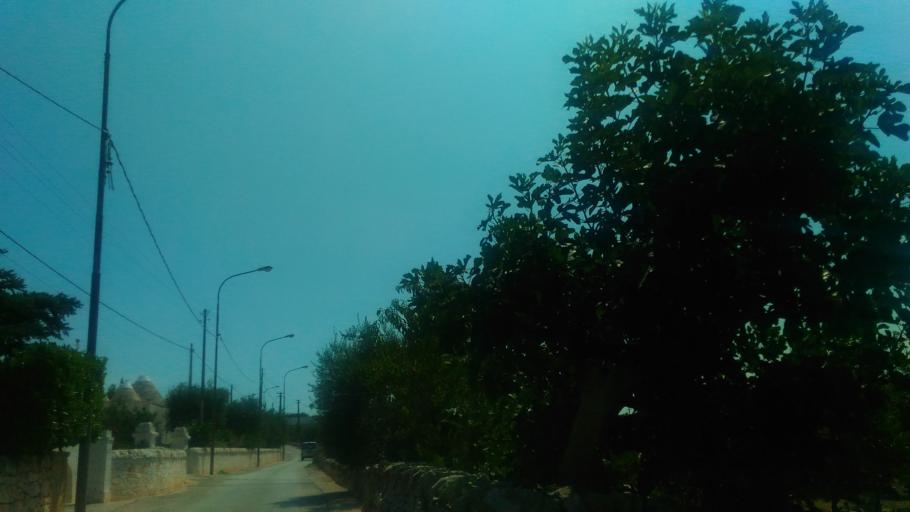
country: IT
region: Apulia
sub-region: Provincia di Bari
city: Locorotondo
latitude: 40.7495
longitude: 17.3711
